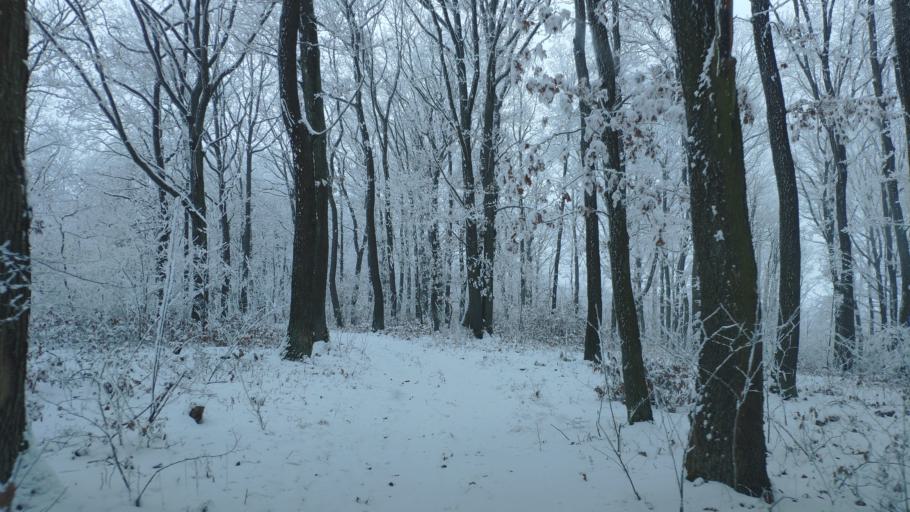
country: SK
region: Kosicky
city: Kosice
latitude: 48.6536
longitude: 21.1833
